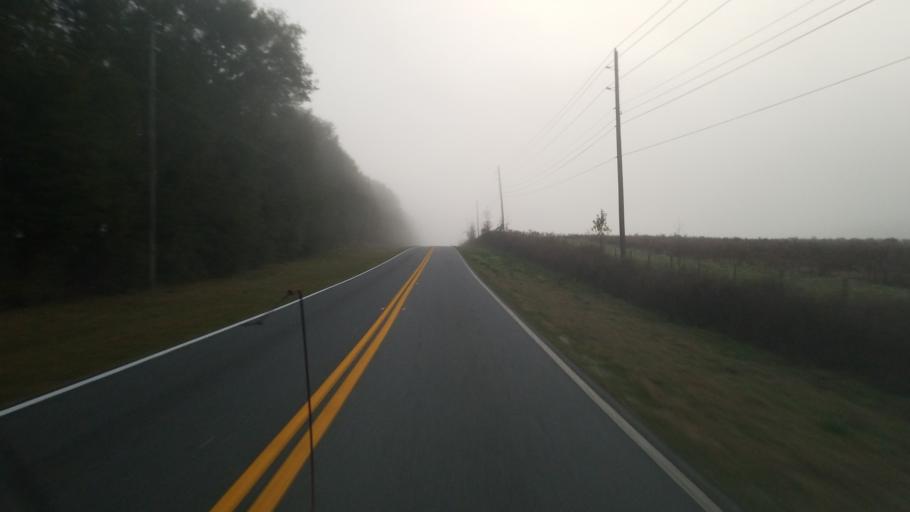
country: US
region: Florida
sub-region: Marion County
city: Ocala
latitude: 29.1502
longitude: -82.2342
